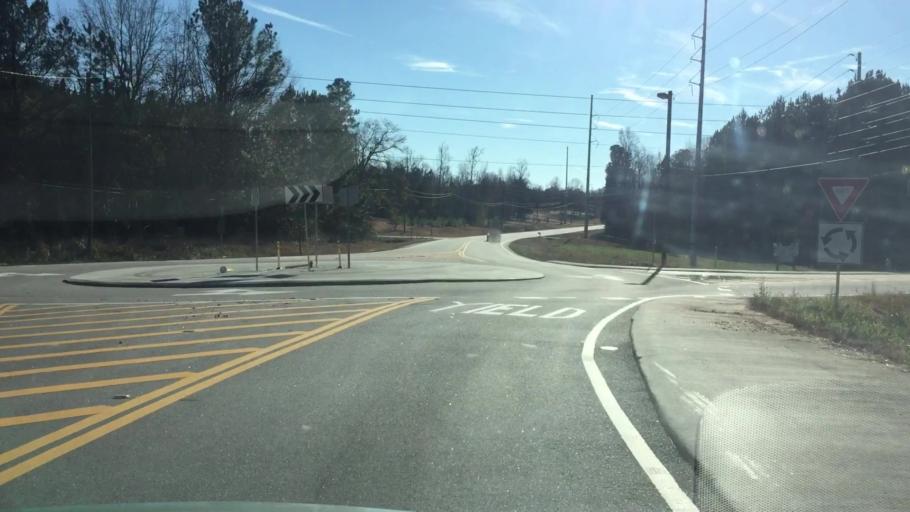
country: US
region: Georgia
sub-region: Newton County
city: Oakwood
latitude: 33.4630
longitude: -83.9686
